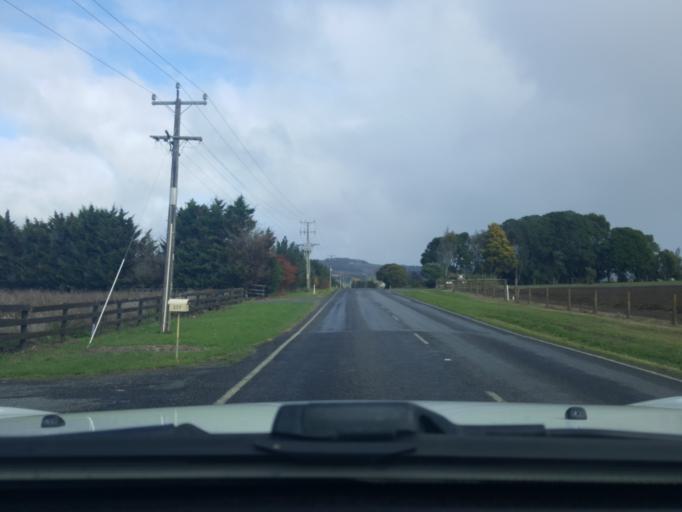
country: NZ
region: Auckland
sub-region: Auckland
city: Pukekohe East
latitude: -37.3015
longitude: 175.0210
